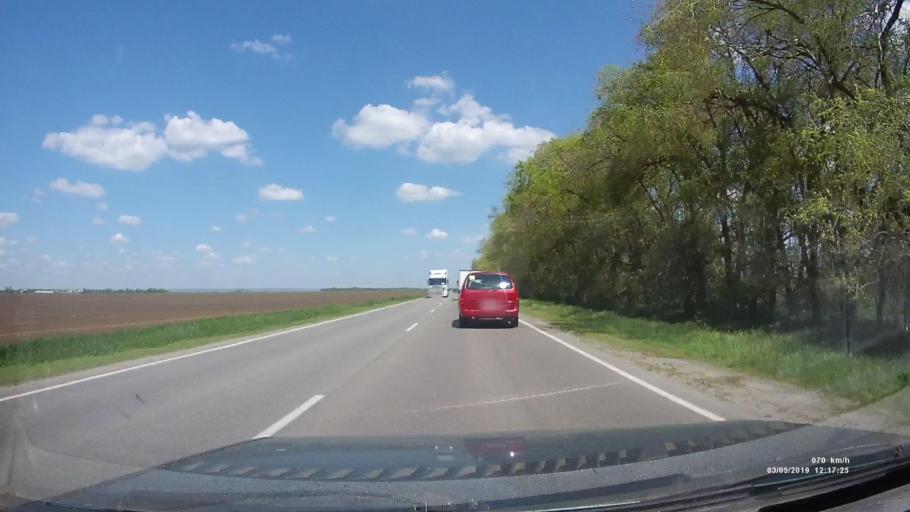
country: RU
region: Rostov
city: Melikhovskaya
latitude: 47.3823
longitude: 40.5920
